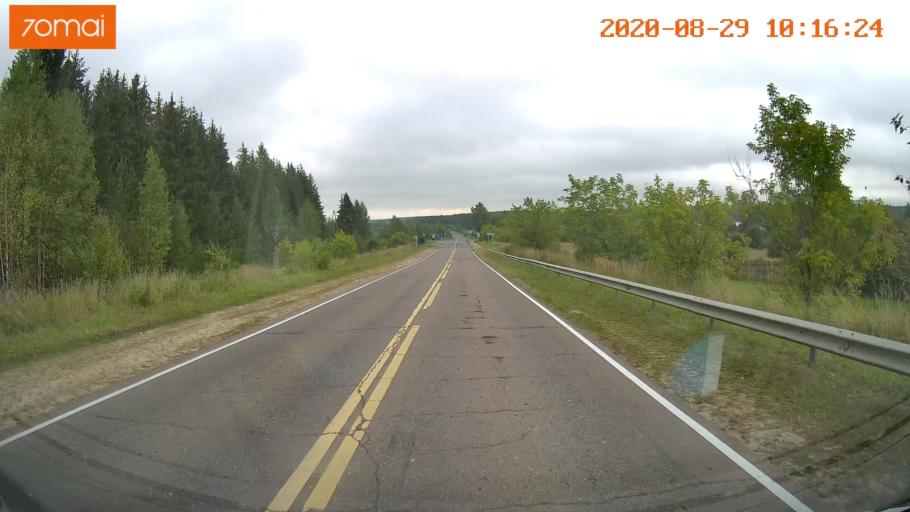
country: RU
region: Ivanovo
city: Yur'yevets
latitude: 57.3384
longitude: 42.7912
